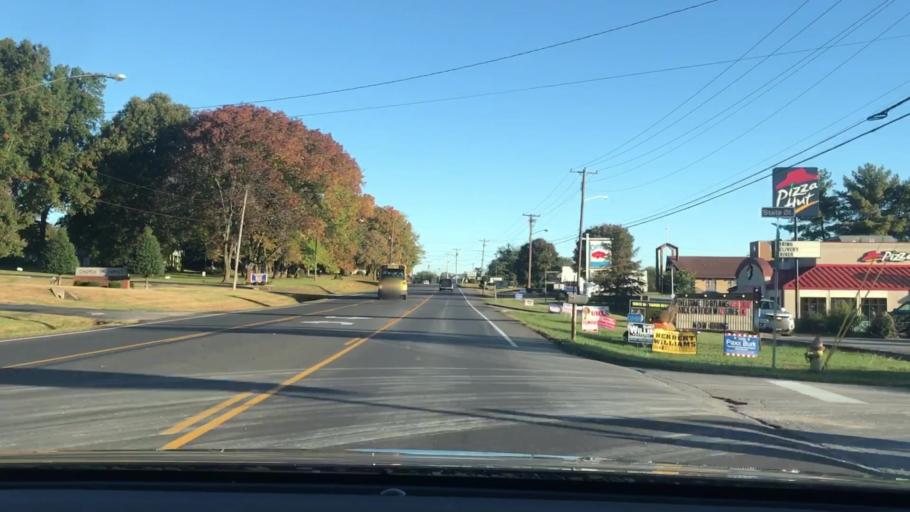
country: US
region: Kentucky
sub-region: Simpson County
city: Franklin
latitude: 36.7100
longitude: -86.5762
